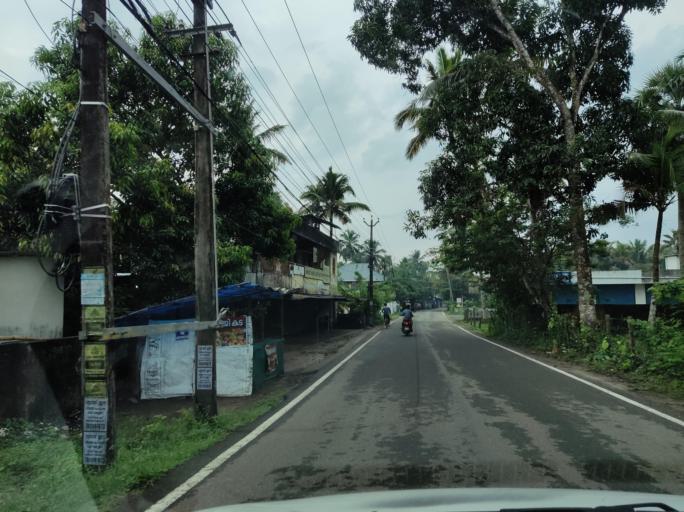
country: IN
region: Kerala
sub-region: Alappuzha
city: Kayankulam
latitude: 9.2453
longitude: 76.4529
